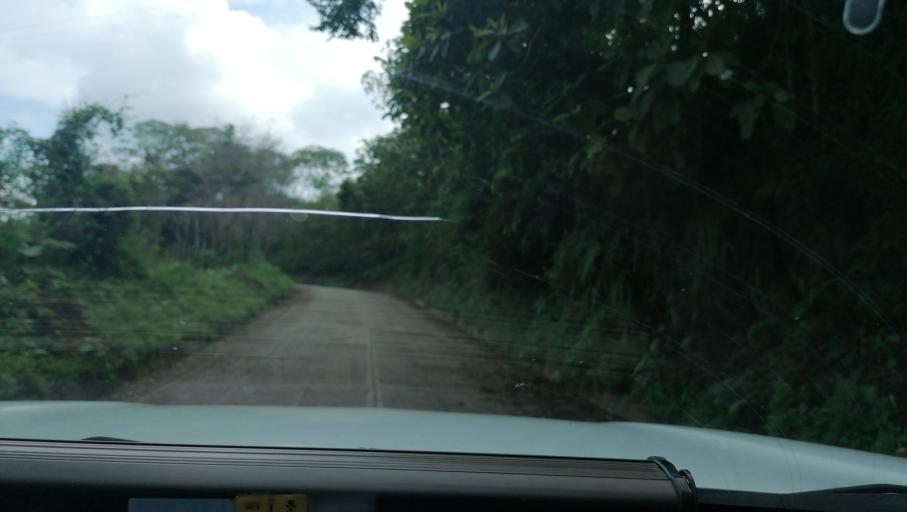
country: MX
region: Chiapas
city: Ixtacomitan
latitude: 17.3366
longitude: -93.1109
